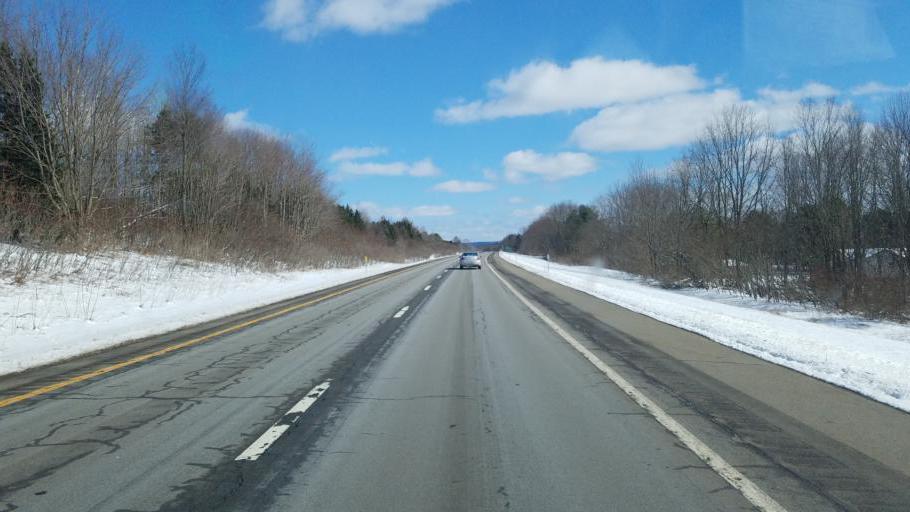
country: US
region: New York
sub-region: Chautauqua County
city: Falconer
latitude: 42.1373
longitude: -79.1618
